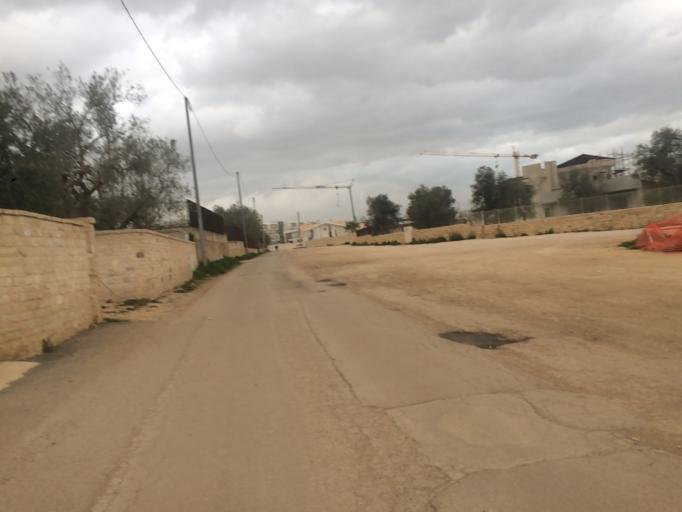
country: IT
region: Apulia
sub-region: Provincia di Bari
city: Terlizzi
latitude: 41.1267
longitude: 16.5607
